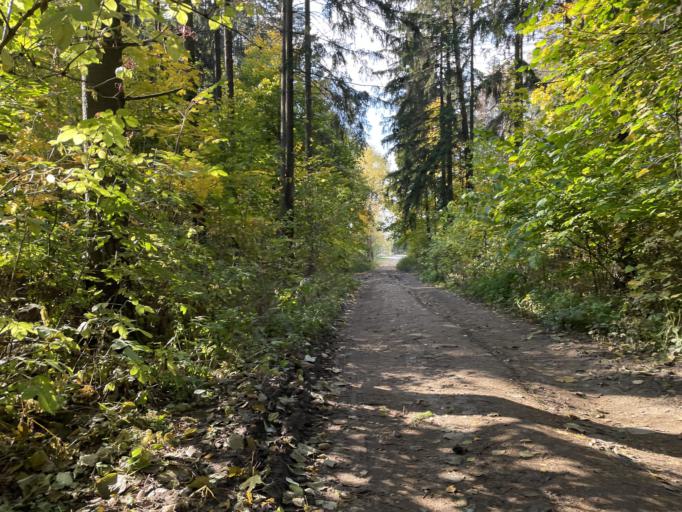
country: BY
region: Minsk
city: Minsk
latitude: 53.9097
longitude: 27.6152
